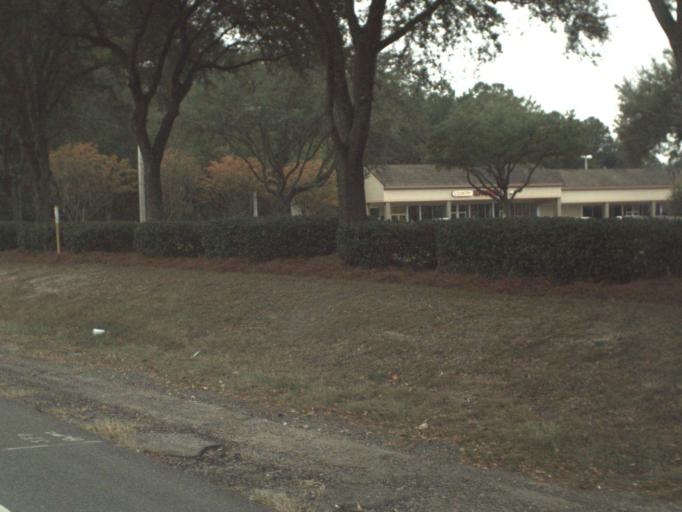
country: US
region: Florida
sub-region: Gadsden County
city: Midway
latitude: 30.5313
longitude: -84.3621
